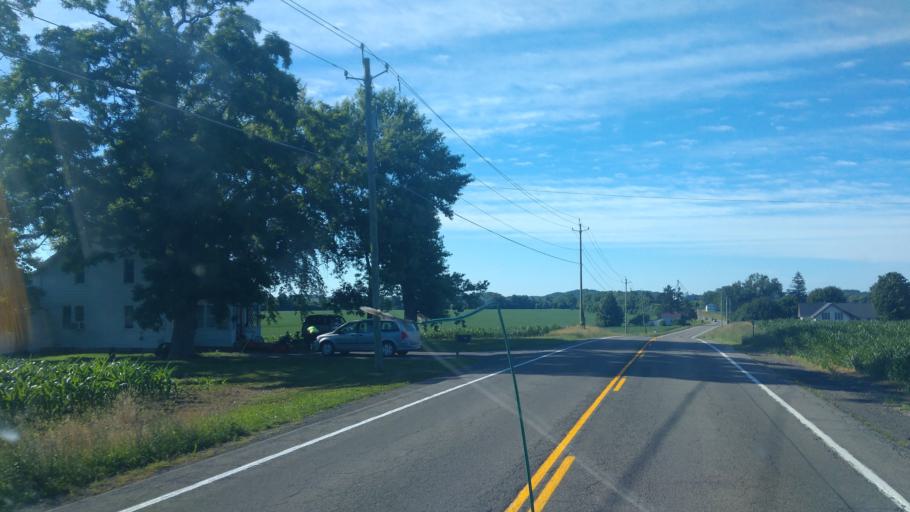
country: US
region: New York
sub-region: Wayne County
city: Lyons
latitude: 43.0301
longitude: -76.9915
